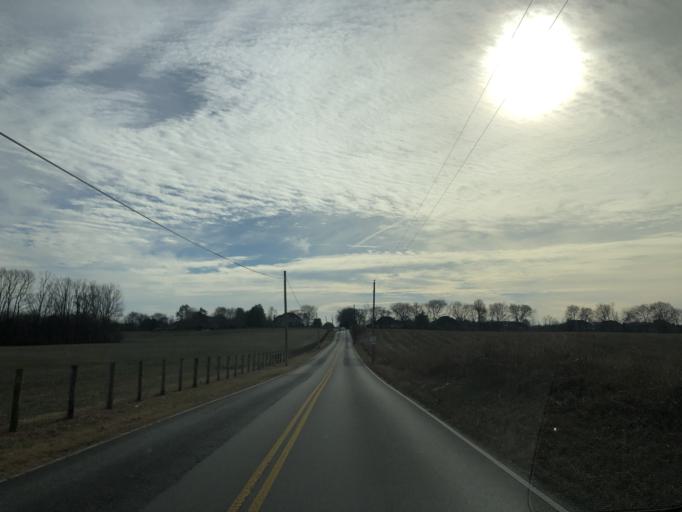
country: US
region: Tennessee
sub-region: Williamson County
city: Franklin
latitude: 35.9572
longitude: -86.9056
